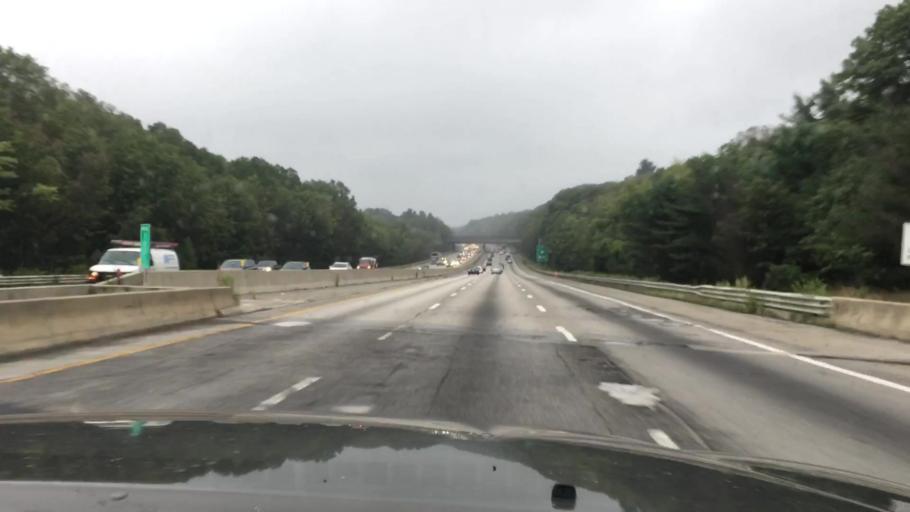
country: US
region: Massachusetts
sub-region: Worcester County
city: Westborough
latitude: 42.2334
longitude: -71.6092
